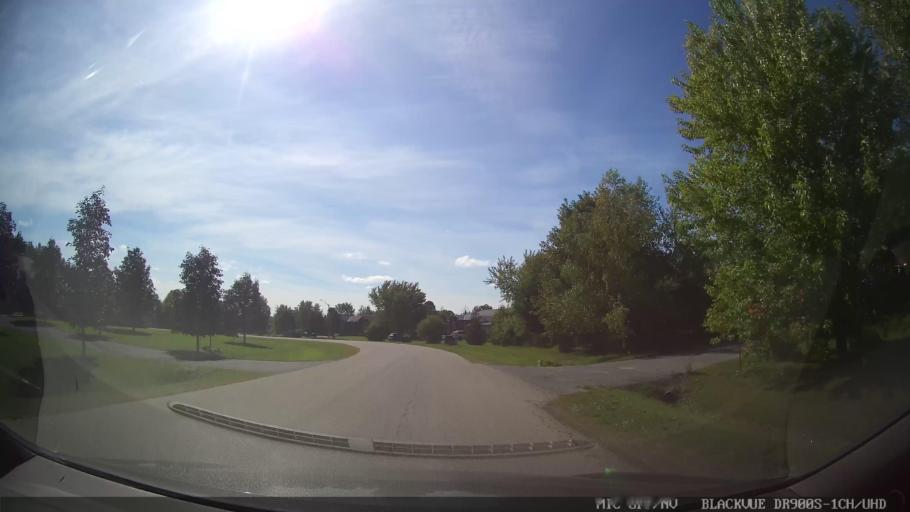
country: CA
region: Ontario
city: Bells Corners
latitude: 45.0936
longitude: -75.7368
